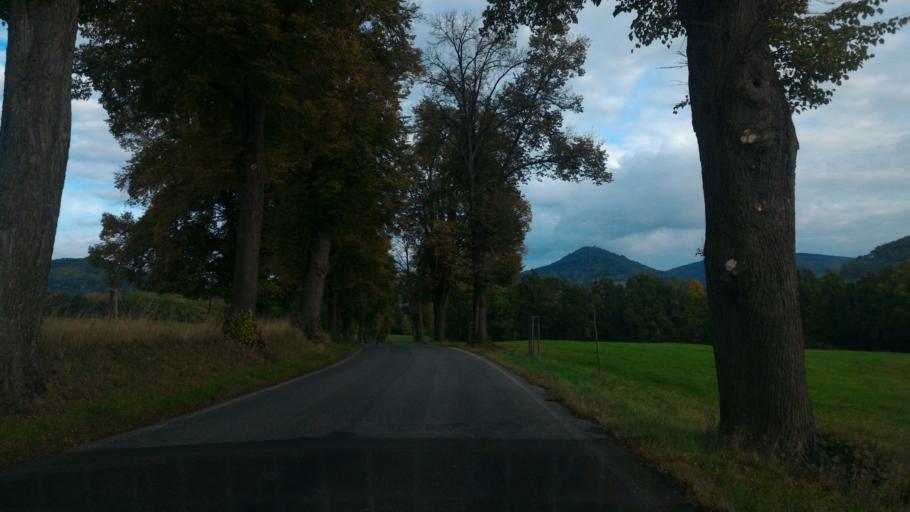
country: CZ
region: Ustecky
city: Ceska Kamenice
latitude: 50.8026
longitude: 14.3942
